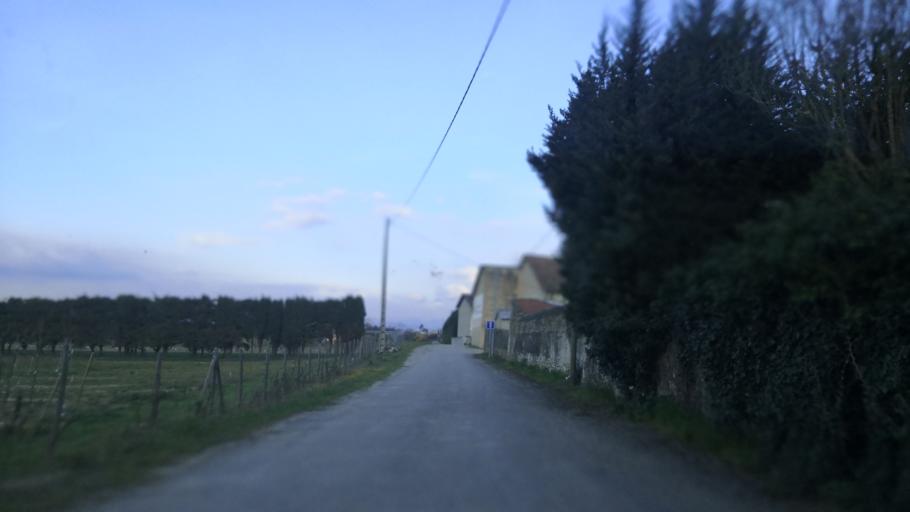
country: FR
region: Rhone-Alpes
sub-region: Departement de la Drome
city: Montboucher-sur-Jabron
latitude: 44.5618
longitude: 4.7855
